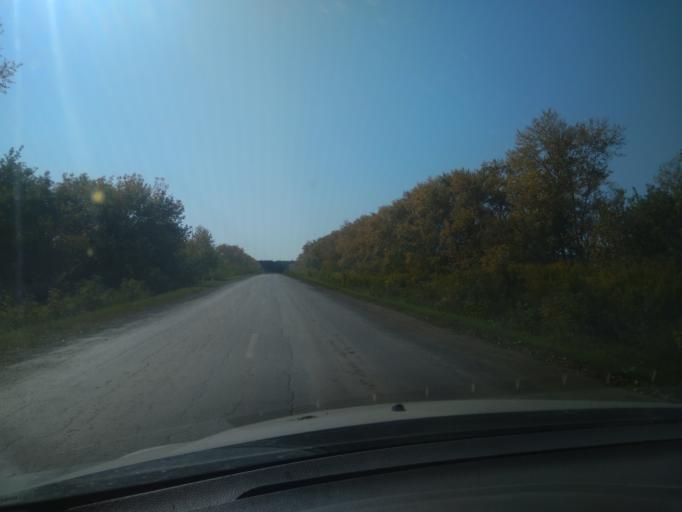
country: RU
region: Sverdlovsk
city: Pokrovskoye
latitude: 56.4601
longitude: 61.6105
